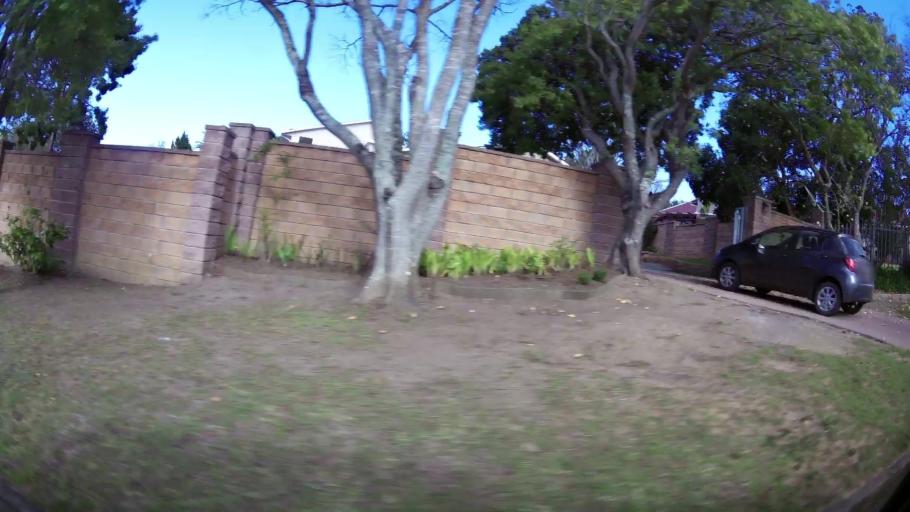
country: ZA
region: Western Cape
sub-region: Eden District Municipality
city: George
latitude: -33.9605
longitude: 22.4961
